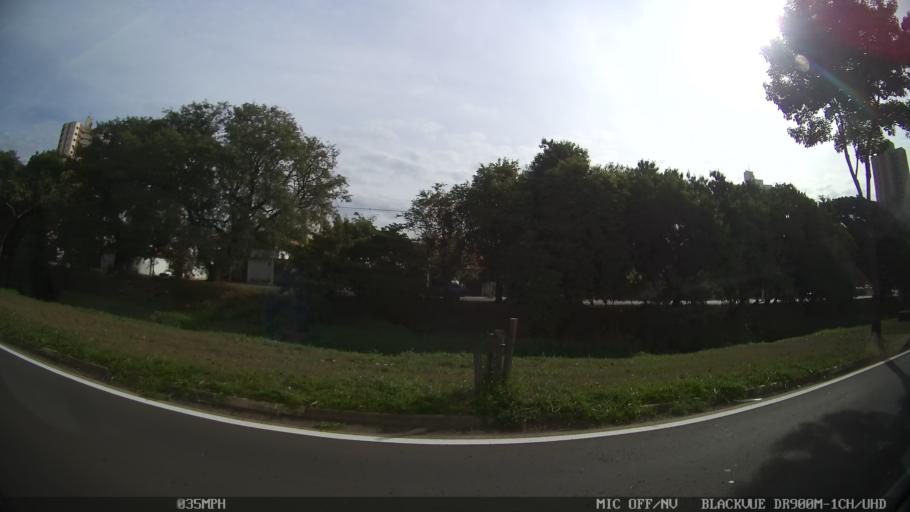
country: BR
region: Sao Paulo
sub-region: Piracicaba
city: Piracicaba
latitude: -22.7280
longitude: -47.6271
